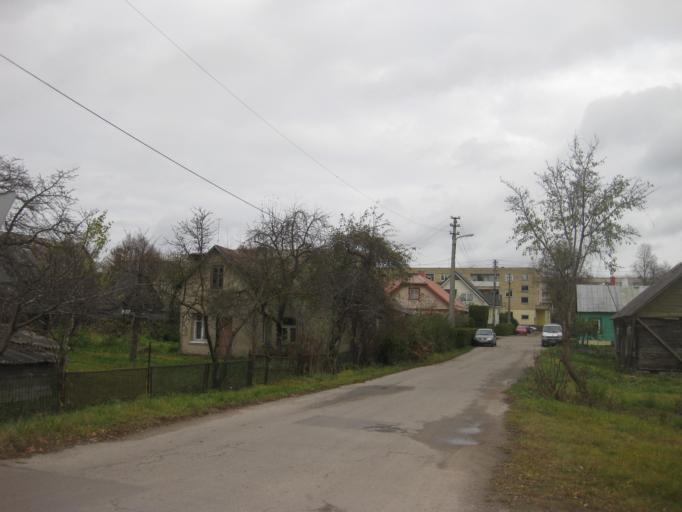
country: LT
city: Prienai
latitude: 54.6361
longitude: 23.9427
